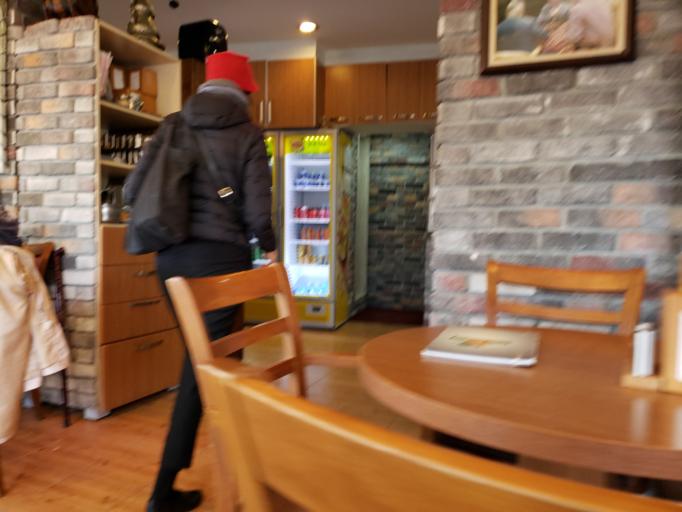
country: TR
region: Istanbul
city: Adalan
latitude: 40.8785
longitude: 29.1000
